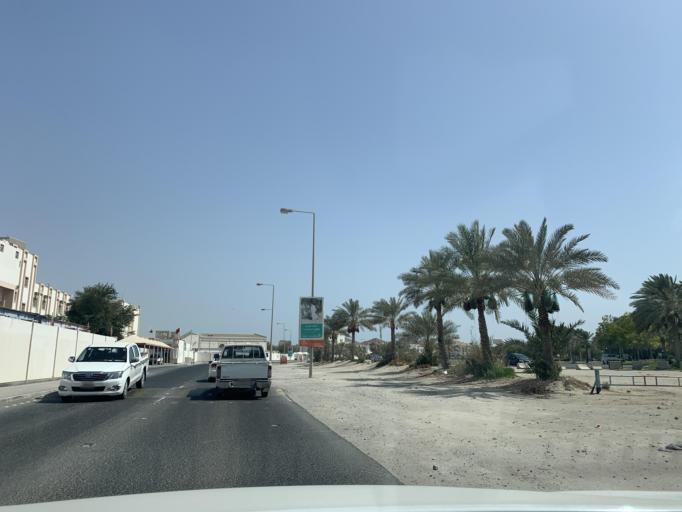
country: BH
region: Manama
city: Jidd Hafs
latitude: 26.2259
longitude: 50.4620
